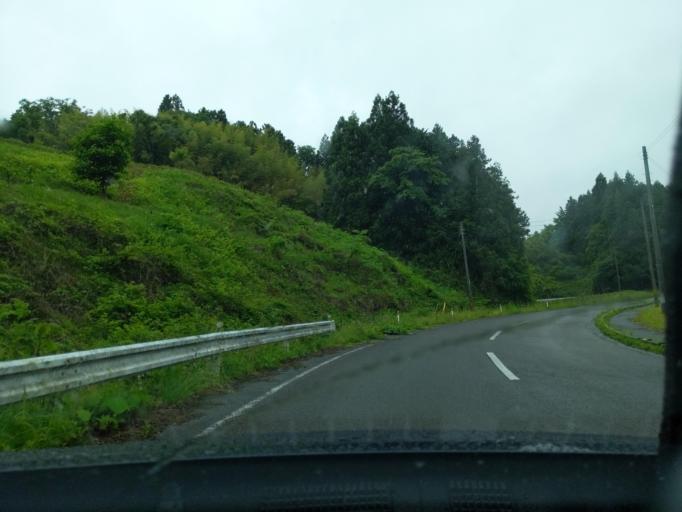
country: JP
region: Fukushima
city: Nihommatsu
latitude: 37.5600
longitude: 140.5359
